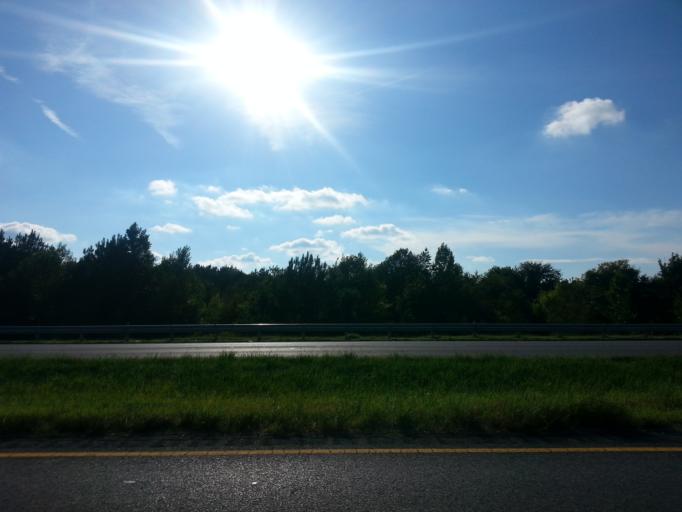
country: US
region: Alabama
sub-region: Colbert County
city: Muscle Shoals
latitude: 34.7239
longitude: -87.6678
